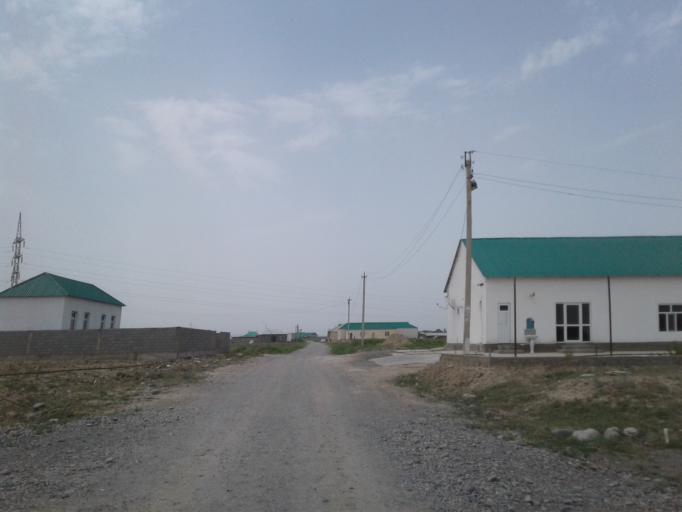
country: TM
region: Ahal
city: Ashgabat
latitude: 37.9805
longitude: 58.3204
